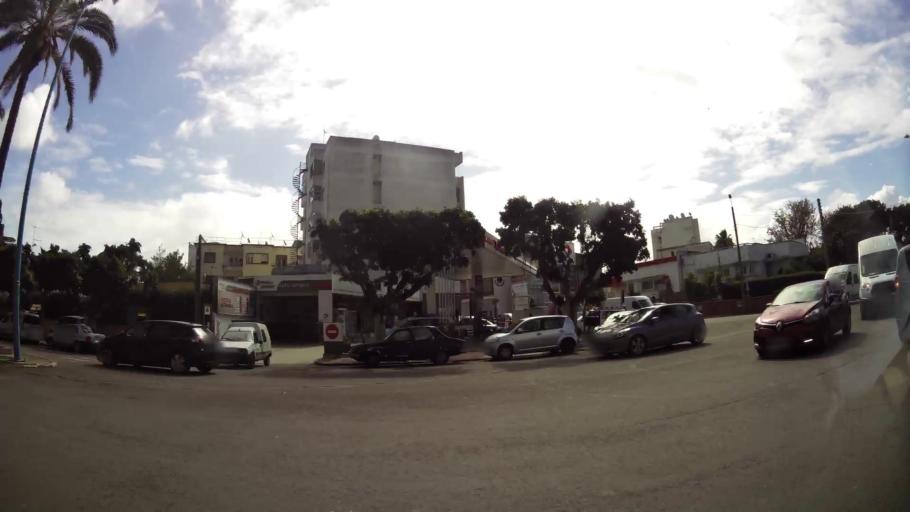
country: MA
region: Grand Casablanca
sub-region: Casablanca
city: Casablanca
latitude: 33.5809
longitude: -7.6322
